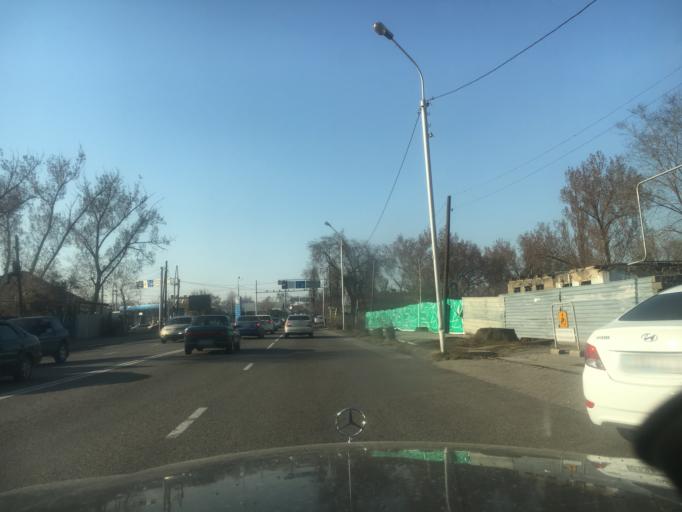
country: KZ
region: Almaty Qalasy
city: Almaty
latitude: 43.2838
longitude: 76.9385
